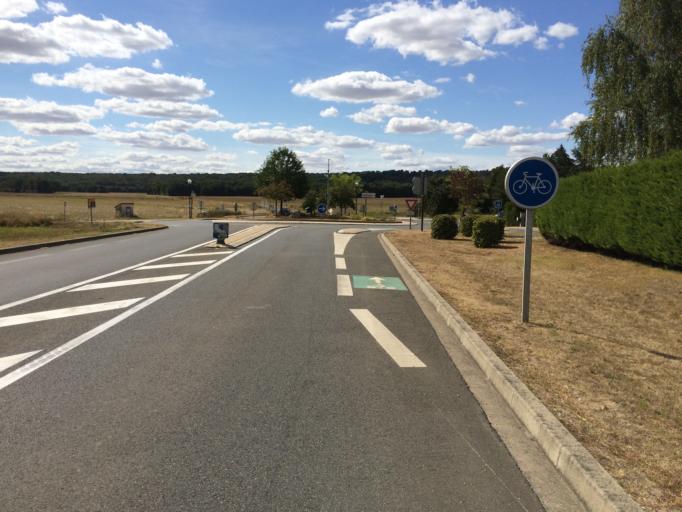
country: FR
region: Ile-de-France
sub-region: Departement de l'Essonne
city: Boutigny-sur-Essonne
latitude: 48.4326
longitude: 2.3586
